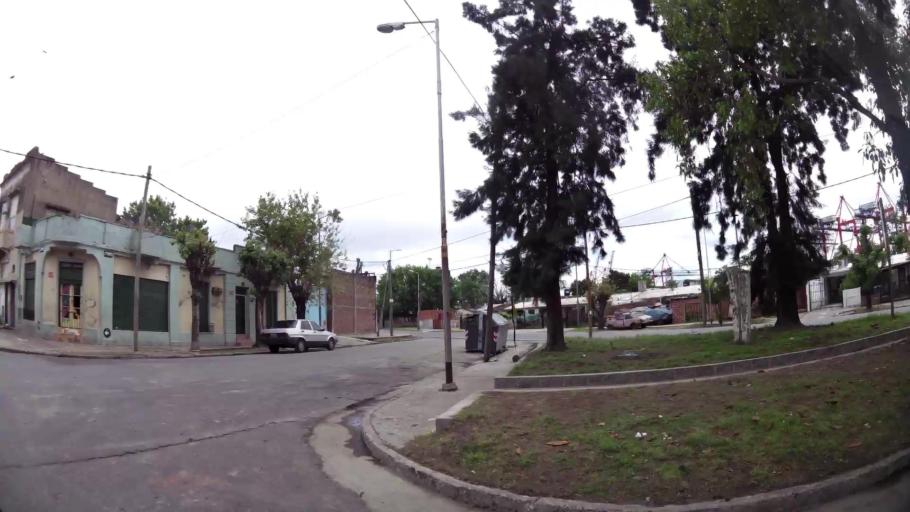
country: AR
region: Buenos Aires
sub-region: Partido de Avellaneda
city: Avellaneda
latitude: -34.6471
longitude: -58.3448
